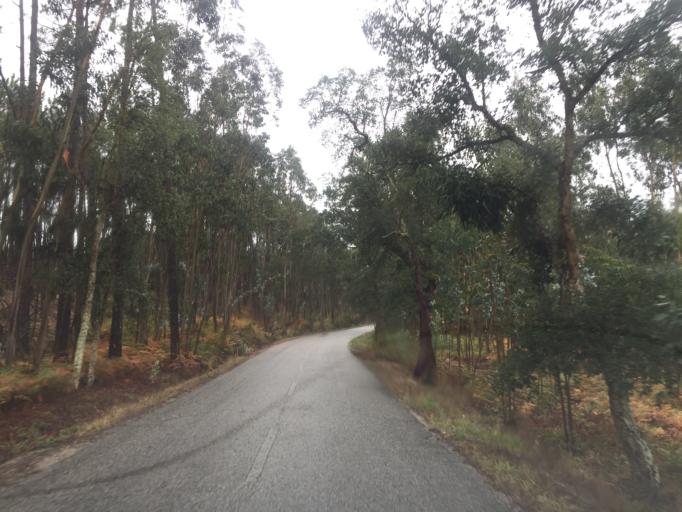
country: PT
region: Leiria
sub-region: Pombal
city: Lourical
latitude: 40.0545
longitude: -8.7735
